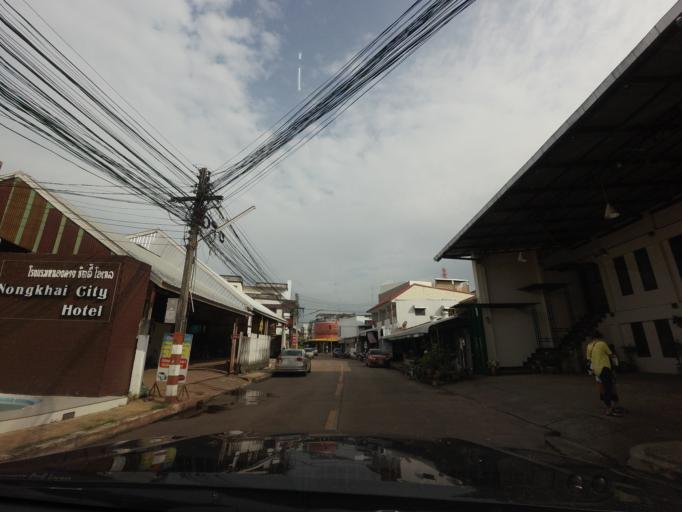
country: TH
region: Nong Khai
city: Nong Khai
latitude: 17.8813
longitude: 102.7474
